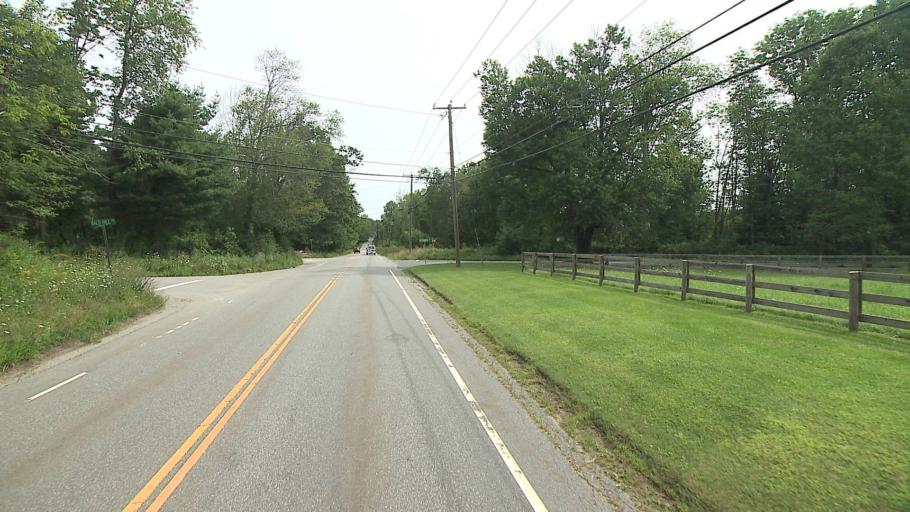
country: US
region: Connecticut
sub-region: Litchfield County
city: Kent
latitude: 41.7192
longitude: -73.4262
